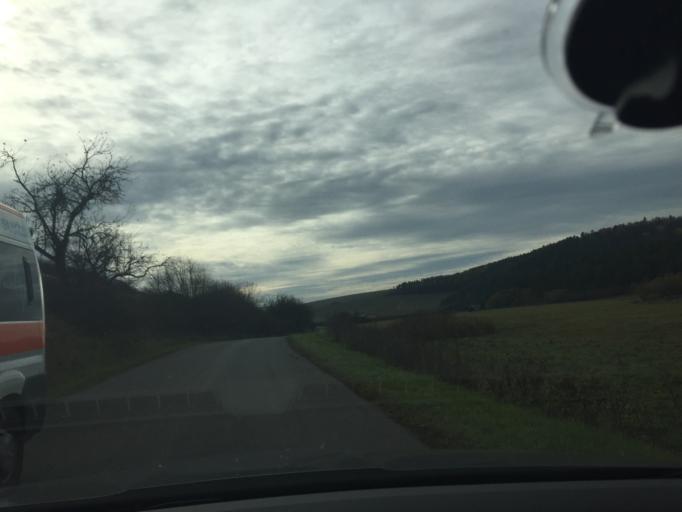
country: SK
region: Presovsky
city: Spisske Podhradie
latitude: 48.9734
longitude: 20.7909
